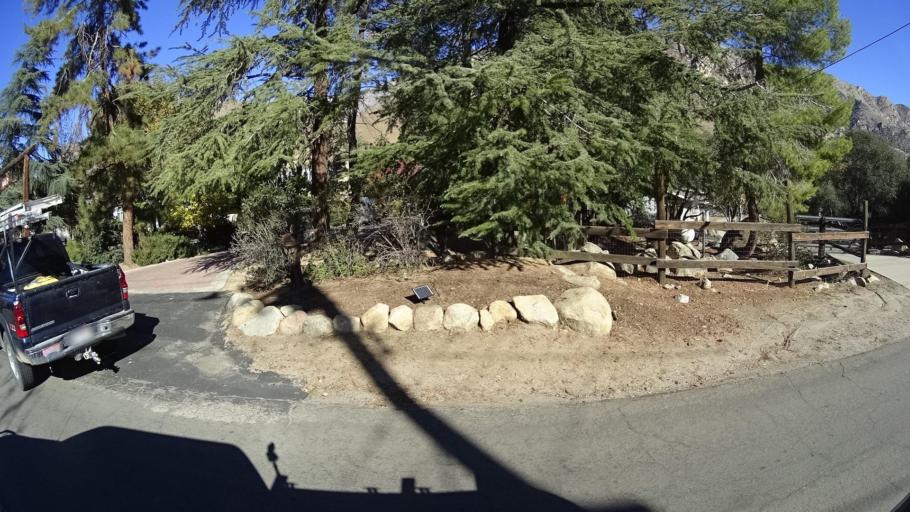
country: US
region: California
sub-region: Kern County
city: Kernville
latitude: 35.7676
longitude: -118.4338
